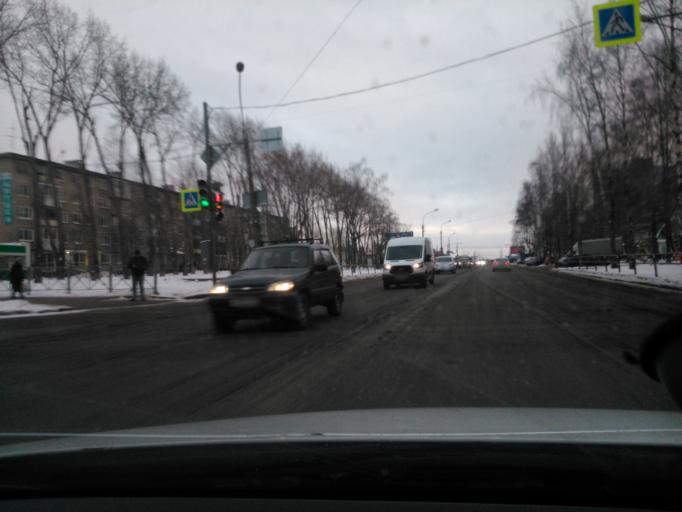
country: RU
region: Perm
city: Kondratovo
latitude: 57.9634
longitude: 56.1788
